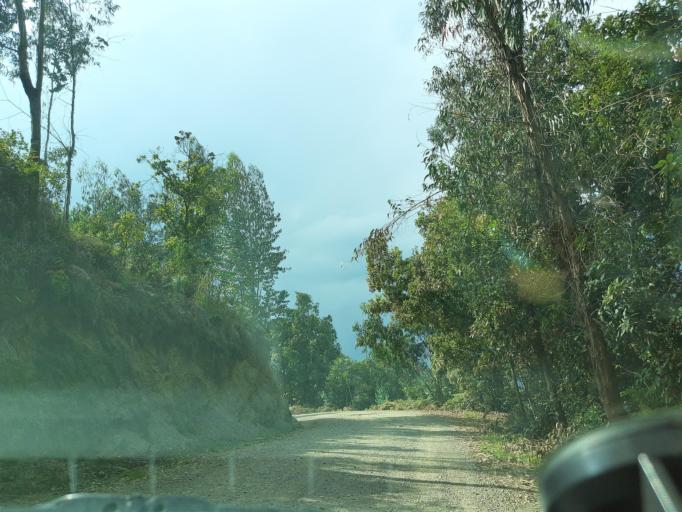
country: CO
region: Boyaca
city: Raquira
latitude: 5.5246
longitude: -73.6671
